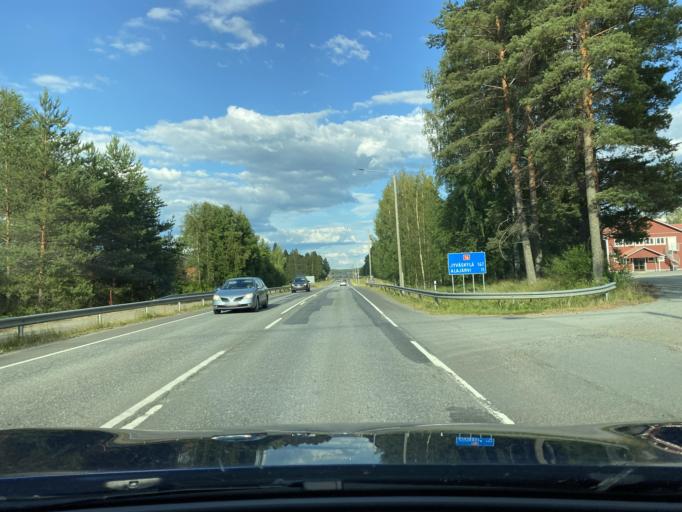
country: FI
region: Southern Ostrobothnia
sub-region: Jaerviseutu
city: Alajaervi
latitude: 63.0155
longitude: 23.6366
